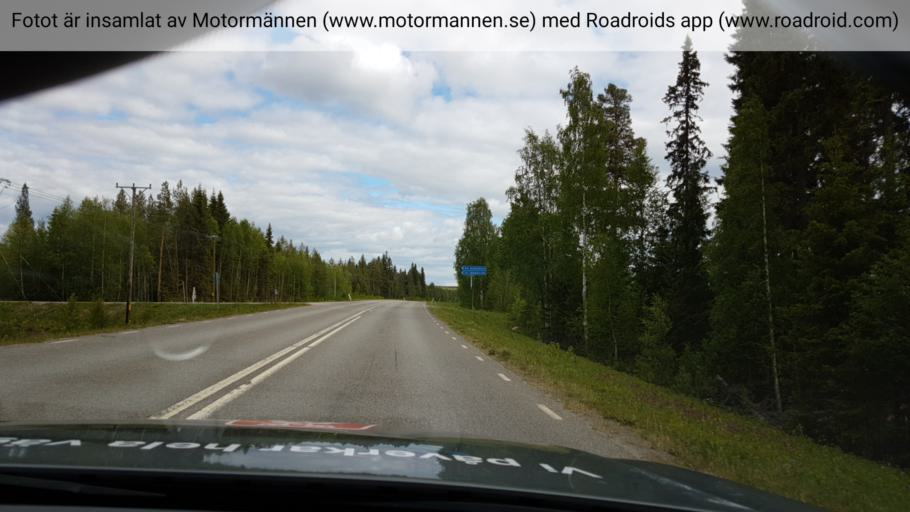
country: SE
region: Jaemtland
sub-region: Stroemsunds Kommun
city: Stroemsund
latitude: 64.3014
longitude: 15.3144
